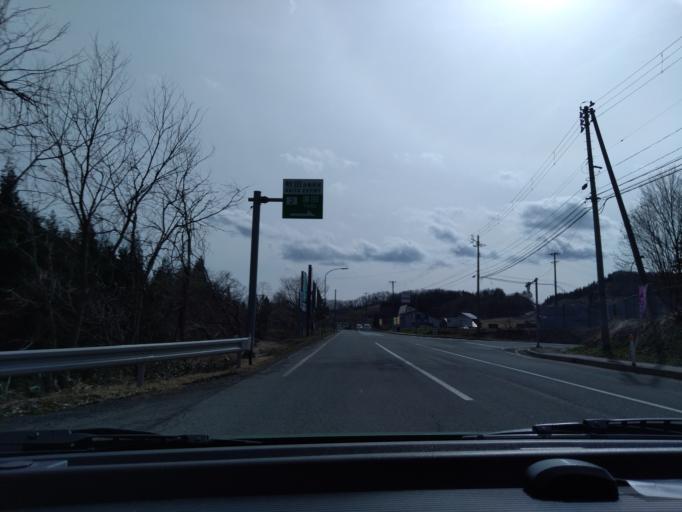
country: JP
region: Akita
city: Yokotemachi
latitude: 39.3112
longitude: 140.7488
